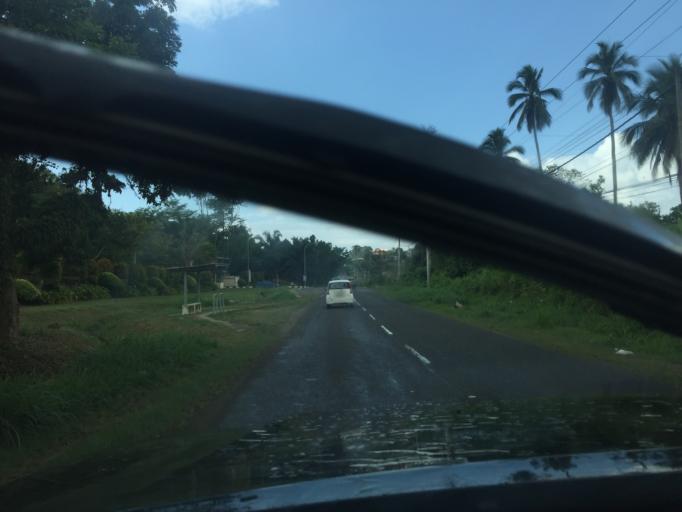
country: MY
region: Sabah
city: Lahad Datu
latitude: 5.0434
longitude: 118.3392
